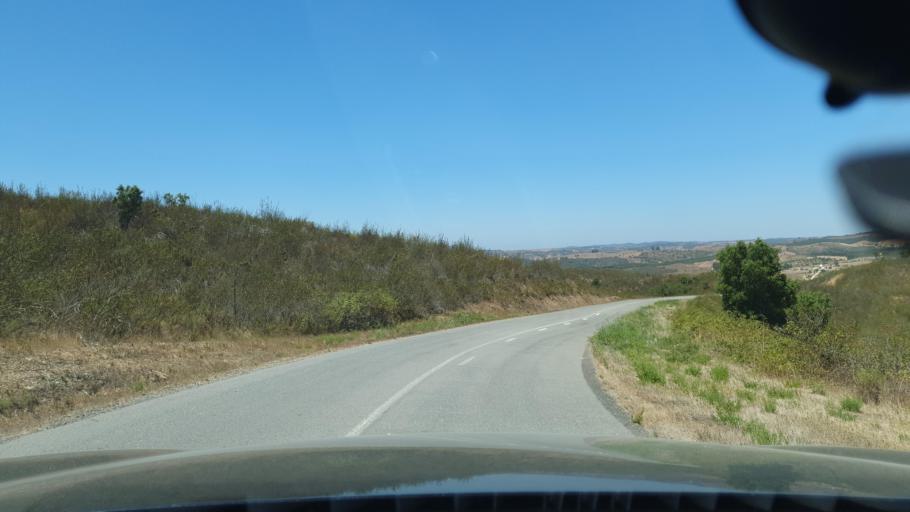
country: PT
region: Beja
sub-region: Odemira
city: Odemira
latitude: 37.5525
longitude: -8.4418
